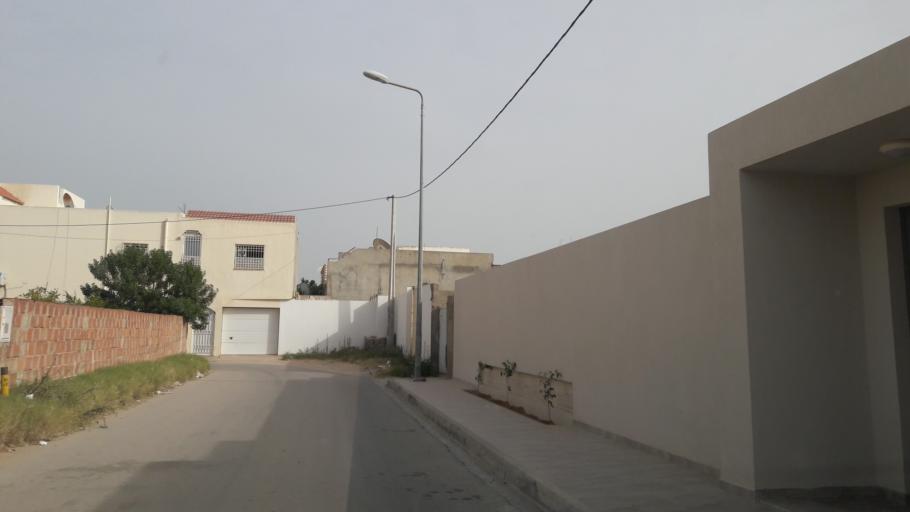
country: TN
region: Safaqis
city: Al Qarmadah
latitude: 34.7786
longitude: 10.7634
